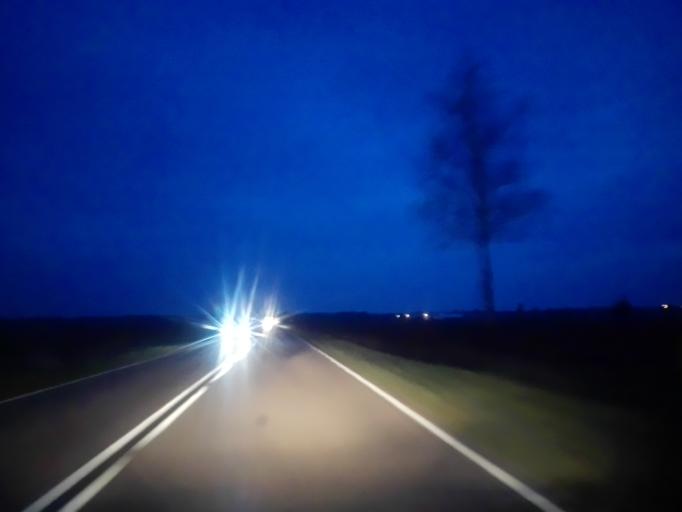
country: PL
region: Podlasie
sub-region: Powiat lomzynski
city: Sniadowo
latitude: 53.0104
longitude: 21.9439
